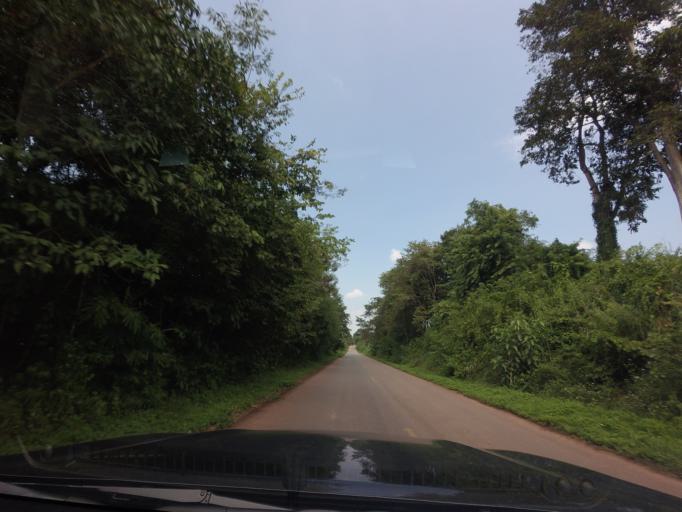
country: TH
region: Uttaradit
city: Fak Tha
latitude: 17.8492
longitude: 100.9556
